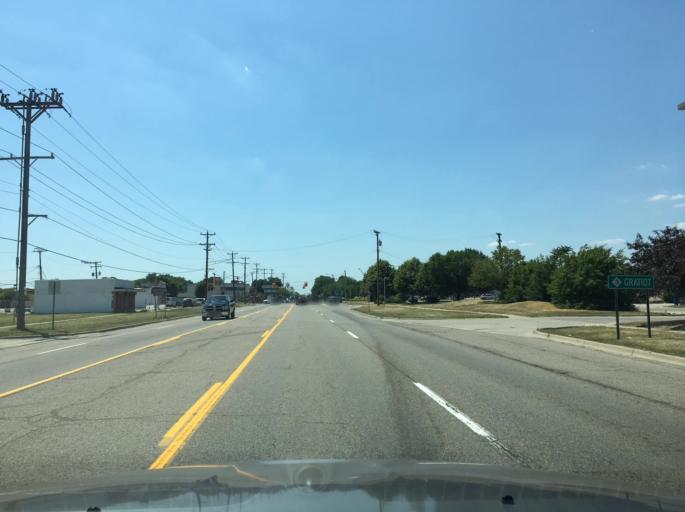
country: US
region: Michigan
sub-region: Macomb County
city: Clinton
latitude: 42.5547
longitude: -82.8974
